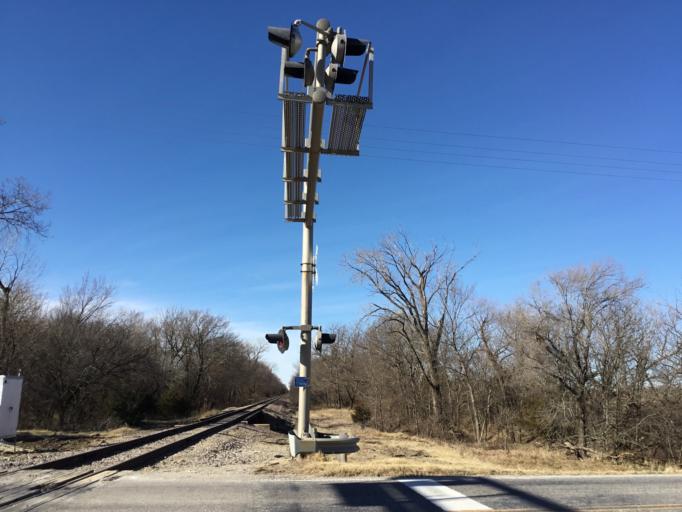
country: US
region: Kansas
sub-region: Butler County
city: Towanda
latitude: 37.7931
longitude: -97.0352
